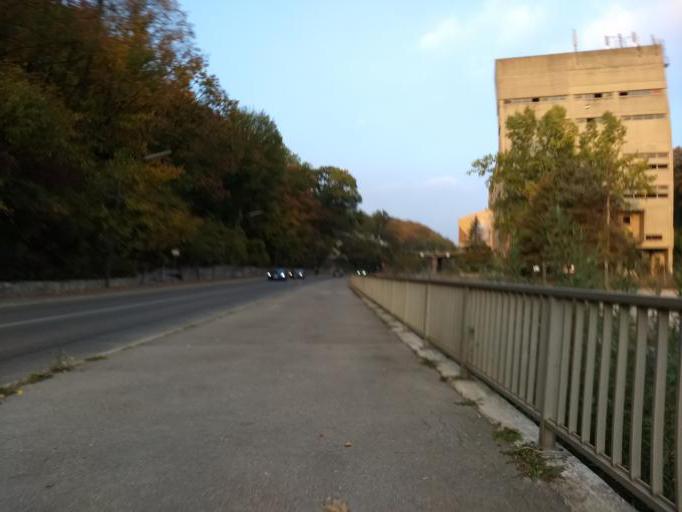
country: AT
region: Lower Austria
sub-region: Politischer Bezirk Modling
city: Kaltenleutgeben
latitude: 48.1260
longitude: 16.2264
